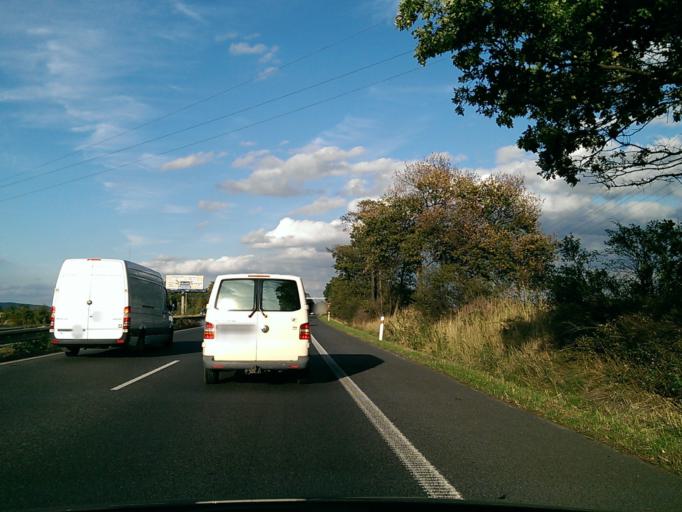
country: CZ
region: Central Bohemia
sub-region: Okres Mlada Boleslav
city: Mlada Boleslav
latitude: 50.3981
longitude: 14.9150
